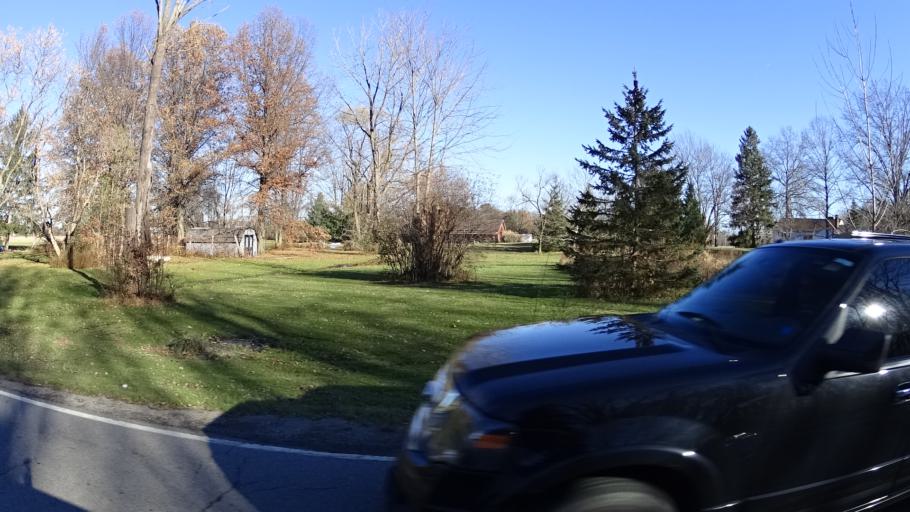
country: US
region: Ohio
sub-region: Lorain County
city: Oberlin
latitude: 41.3093
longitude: -82.1485
